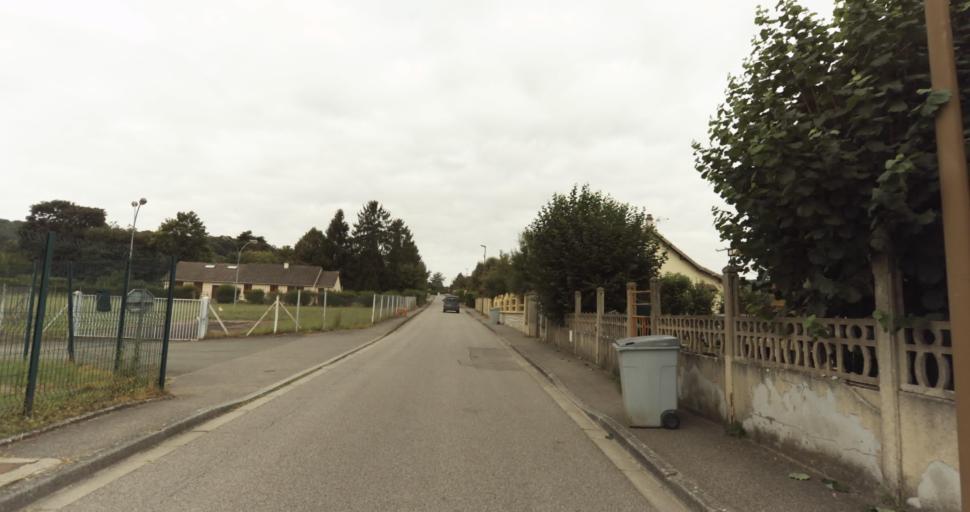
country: FR
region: Haute-Normandie
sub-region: Departement de l'Eure
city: Marcilly-sur-Eure
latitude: 48.8248
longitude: 1.3413
